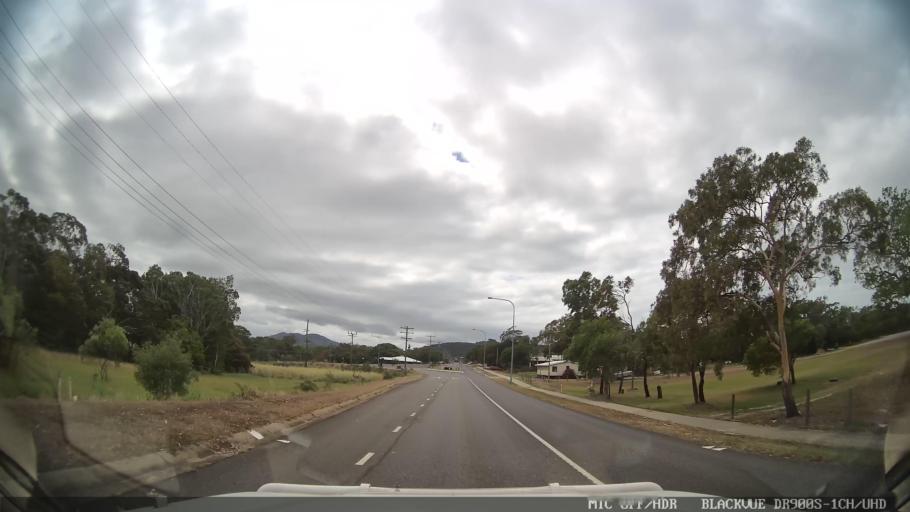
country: AU
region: Queensland
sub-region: Cook
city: Cooktown
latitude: -15.4811
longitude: 145.2483
